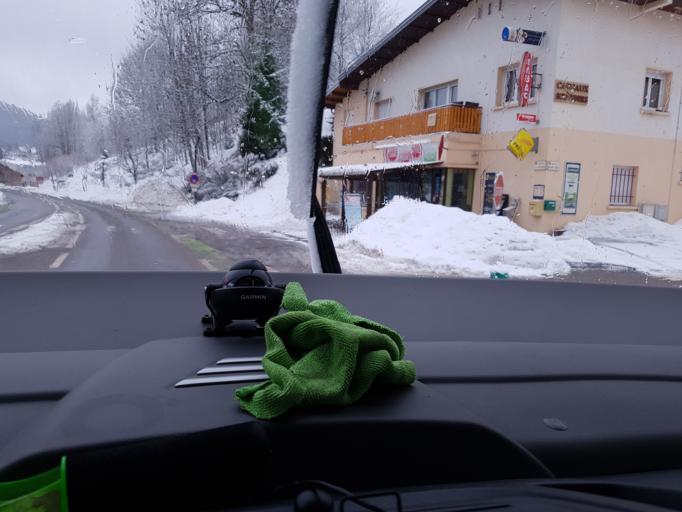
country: FR
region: Lorraine
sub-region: Departement des Vosges
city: Xonrupt-Longemer
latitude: 48.0838
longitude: 6.9266
